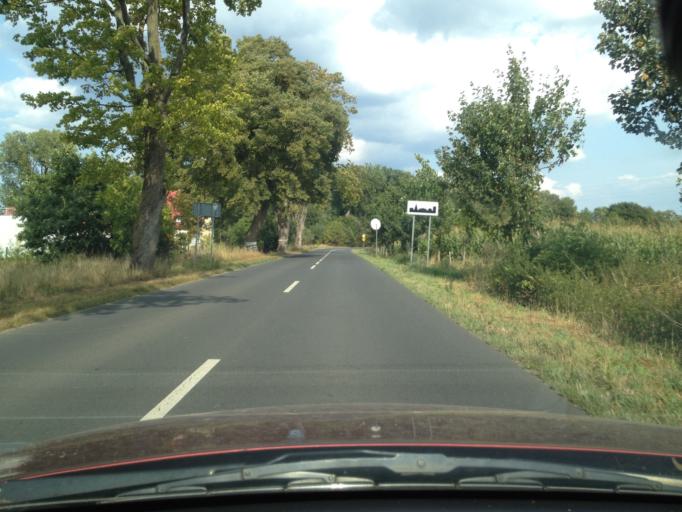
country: PL
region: West Pomeranian Voivodeship
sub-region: Powiat kamienski
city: Dziwnow
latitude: 54.0128
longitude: 14.8516
